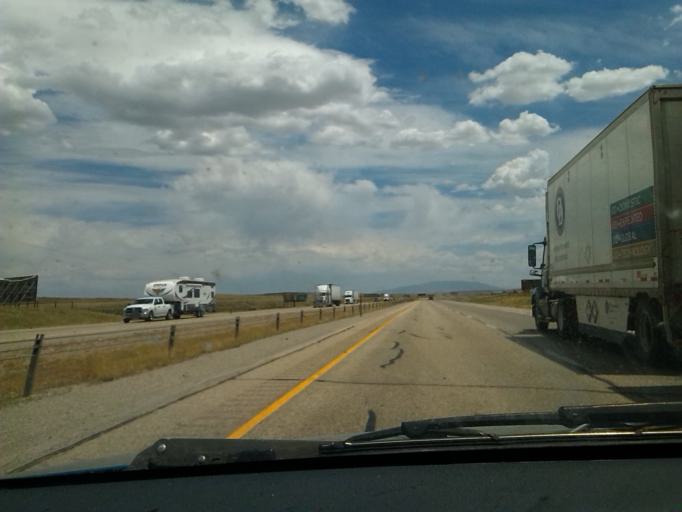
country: US
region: Wyoming
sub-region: Carbon County
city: Rawlins
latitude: 41.7871
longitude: -107.1859
